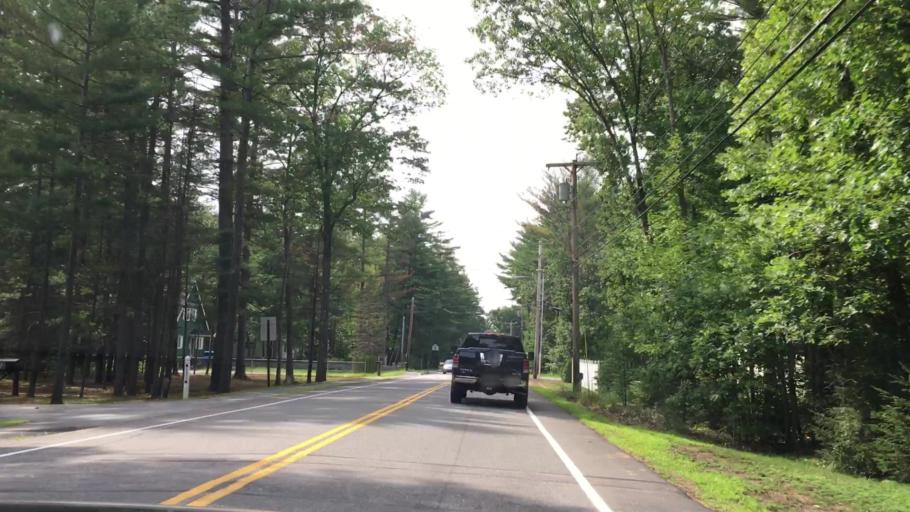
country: US
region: New Hampshire
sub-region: Merrimack County
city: East Concord
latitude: 43.2321
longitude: -71.5193
